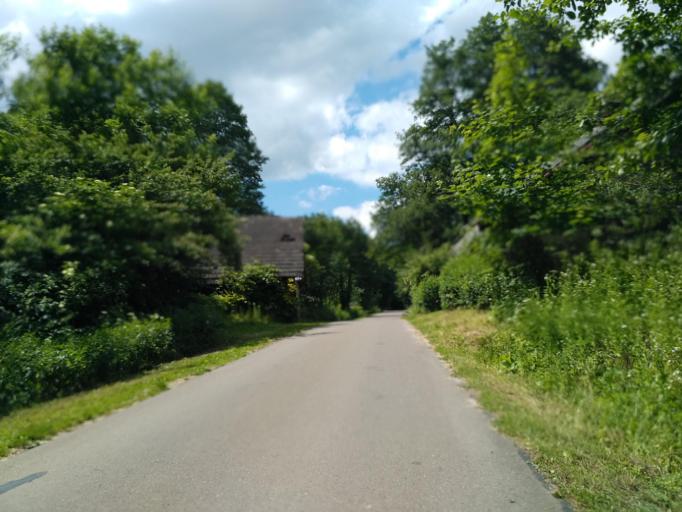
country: PL
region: Subcarpathian Voivodeship
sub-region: Powiat brzozowski
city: Wesola
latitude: 49.7561
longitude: 22.1377
